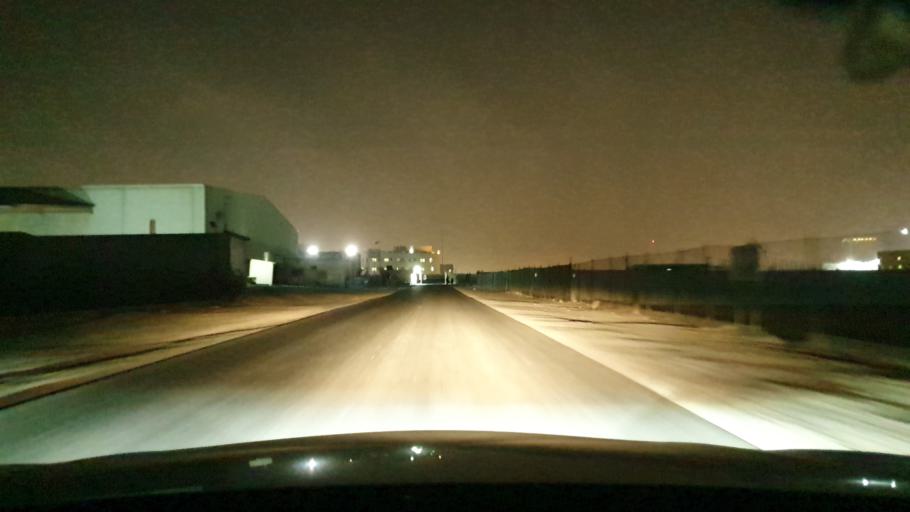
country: BH
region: Northern
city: Sitrah
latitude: 26.0973
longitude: 50.6171
